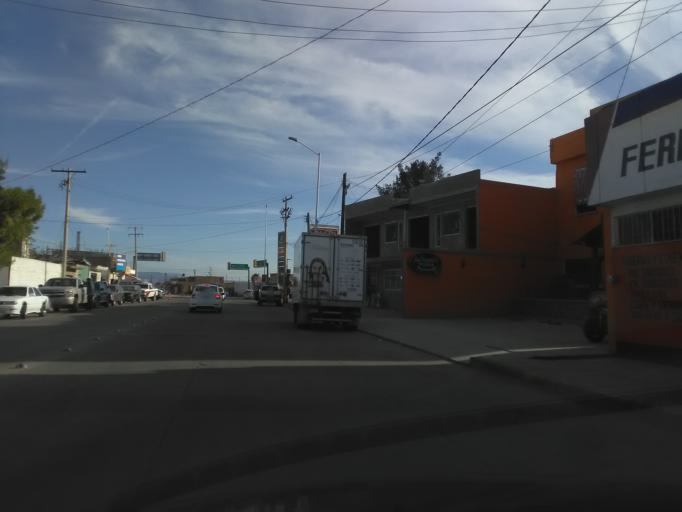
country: MX
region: Durango
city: Victoria de Durango
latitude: 24.0131
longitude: -104.6224
